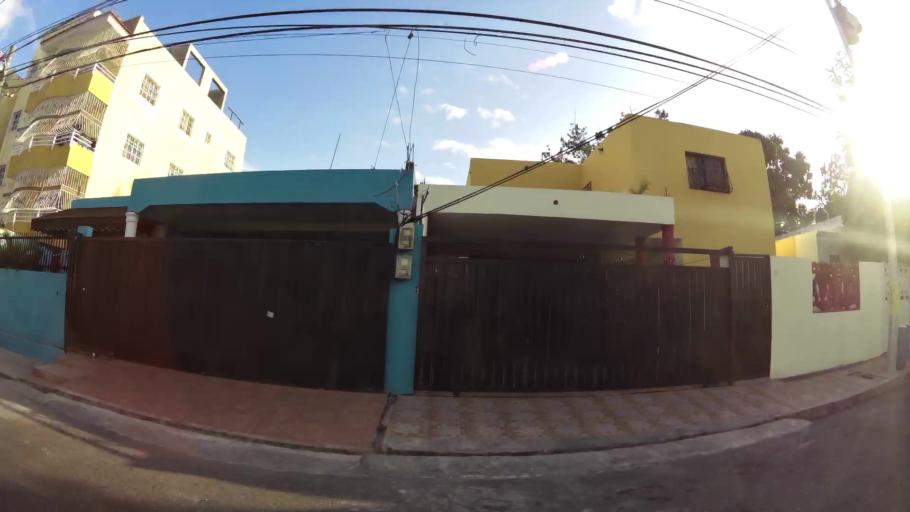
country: DO
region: Nacional
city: Ensanche Luperon
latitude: 18.5446
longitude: -69.9039
